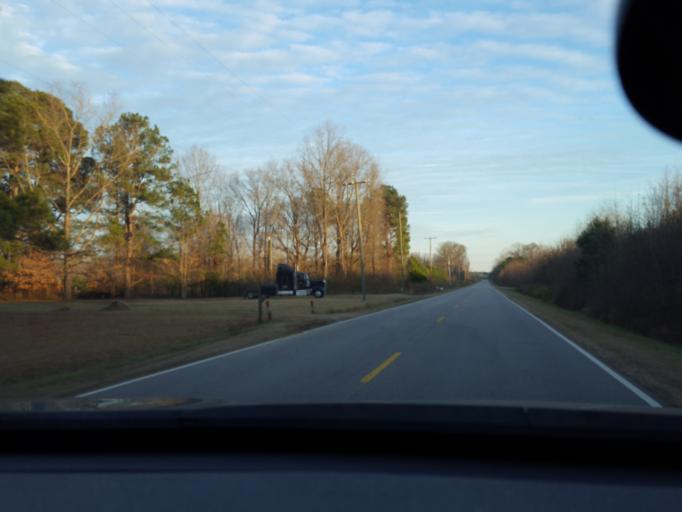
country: US
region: North Carolina
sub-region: Hertford County
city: Murfreesboro
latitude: 36.2838
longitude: -77.1700
